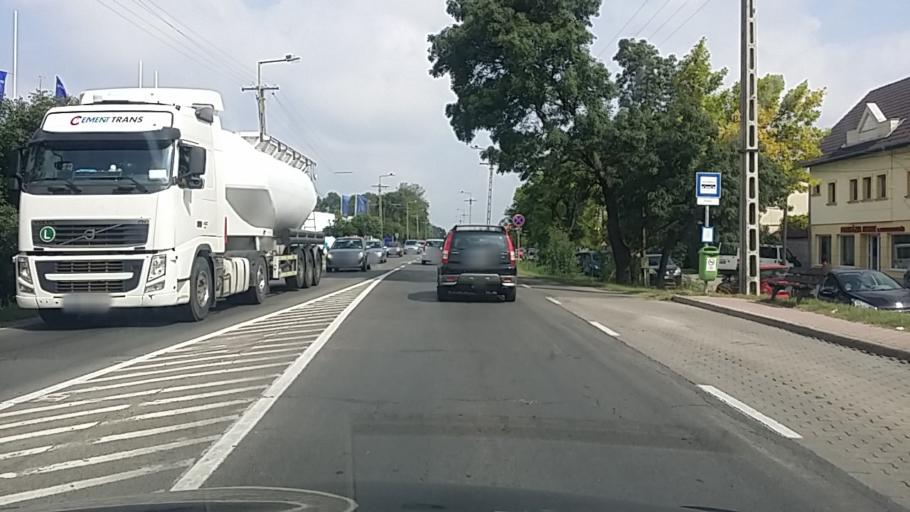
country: HU
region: Csongrad
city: Szeged
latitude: 46.2813
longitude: 20.1690
